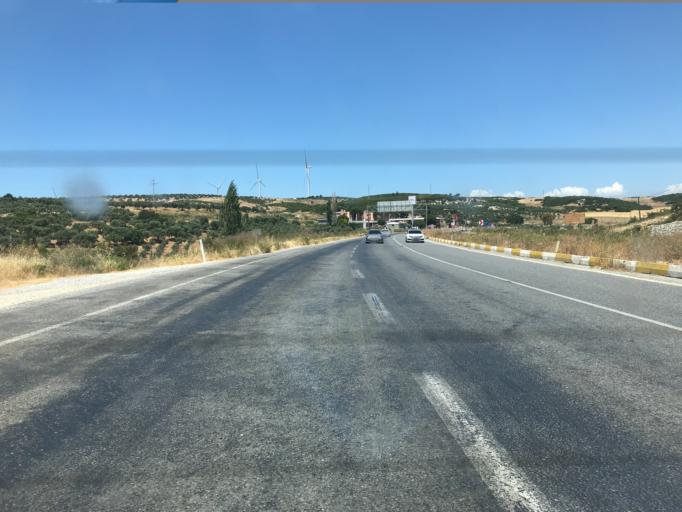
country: TR
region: Aydin
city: Akkoy
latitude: 37.4787
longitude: 27.3406
